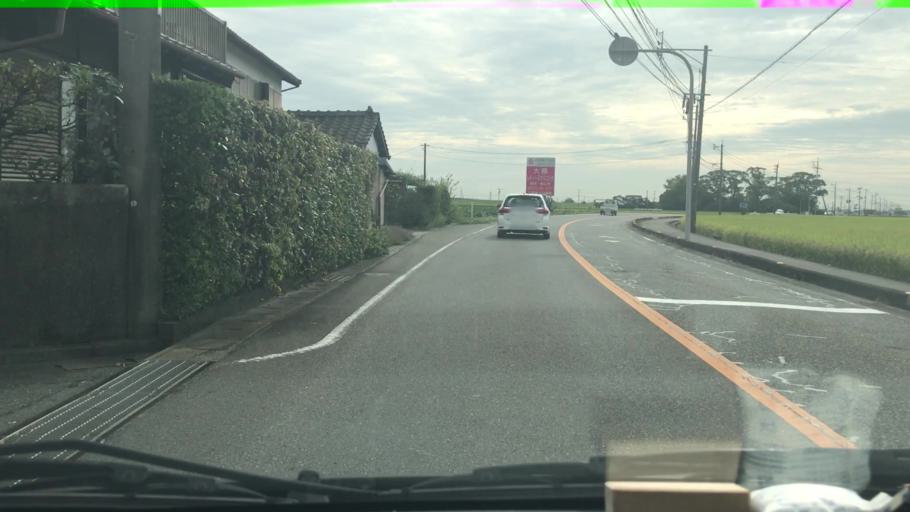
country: JP
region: Saga Prefecture
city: Takeocho-takeo
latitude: 33.2052
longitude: 130.0910
